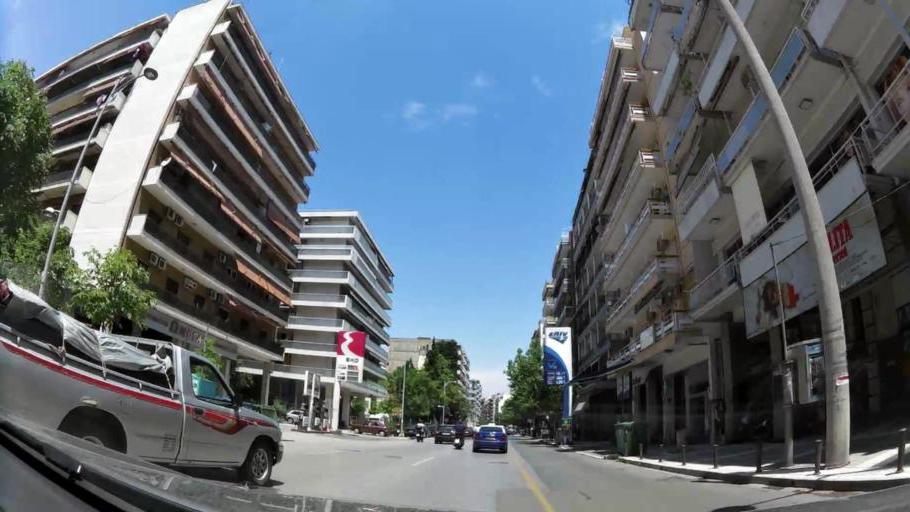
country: GR
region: Central Macedonia
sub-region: Nomos Thessalonikis
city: Triandria
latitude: 40.6146
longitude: 22.9545
